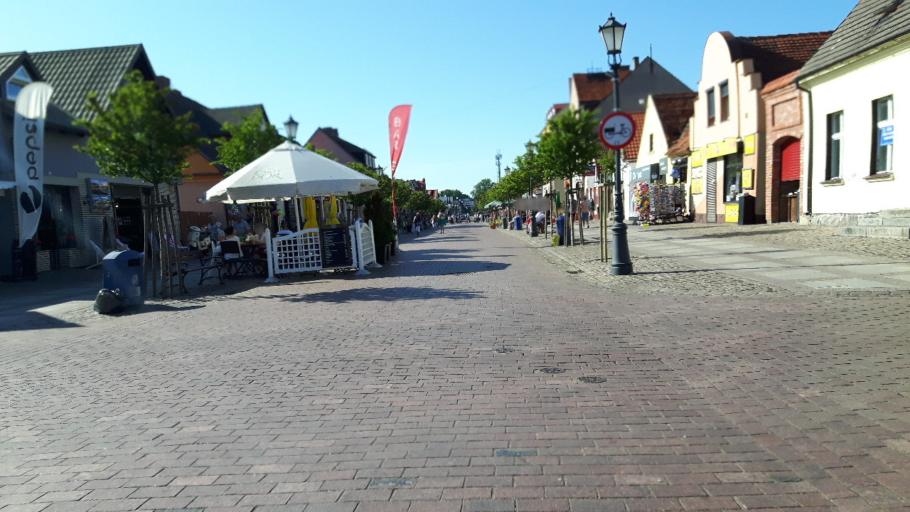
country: PL
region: Pomeranian Voivodeship
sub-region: Powiat leborski
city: Leba
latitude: 54.7575
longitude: 17.5572
